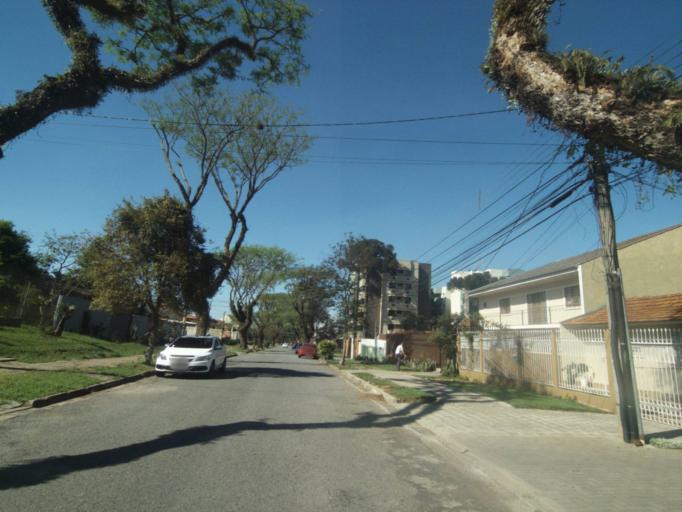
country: BR
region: Parana
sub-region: Curitiba
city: Curitiba
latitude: -25.3965
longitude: -49.2405
